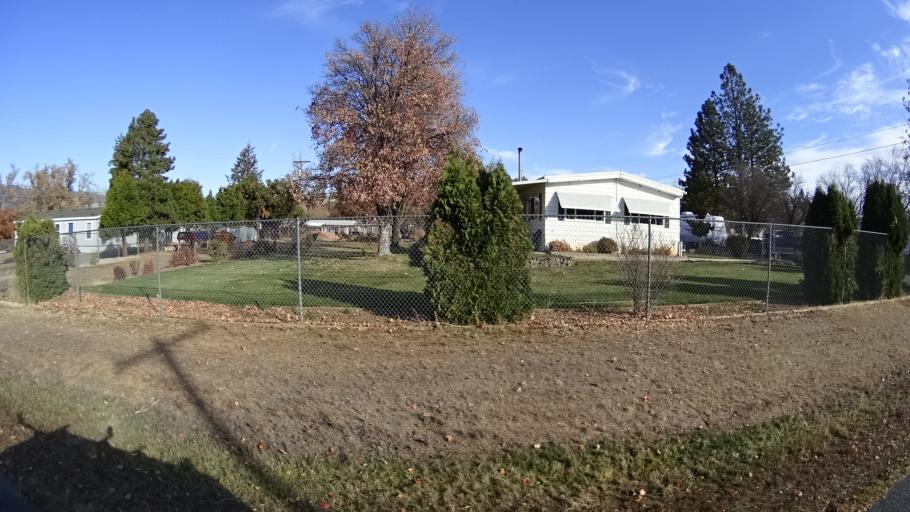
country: US
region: California
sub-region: Siskiyou County
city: Yreka
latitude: 41.6976
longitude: -122.6360
